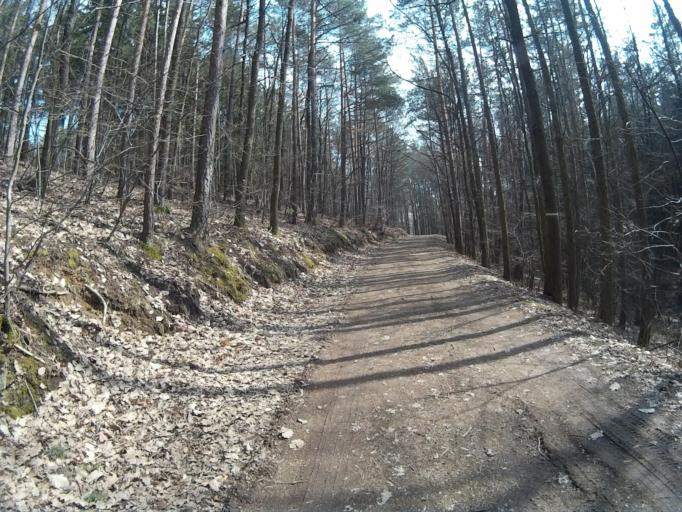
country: CZ
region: South Moravian
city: Pozorice
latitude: 49.2220
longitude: 16.7923
